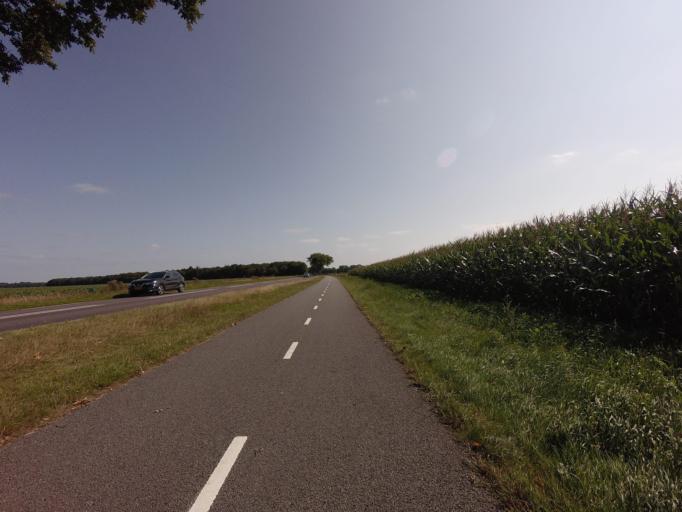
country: NL
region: Drenthe
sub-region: Gemeente Tynaarlo
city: Vries
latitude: 53.0903
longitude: 6.5558
